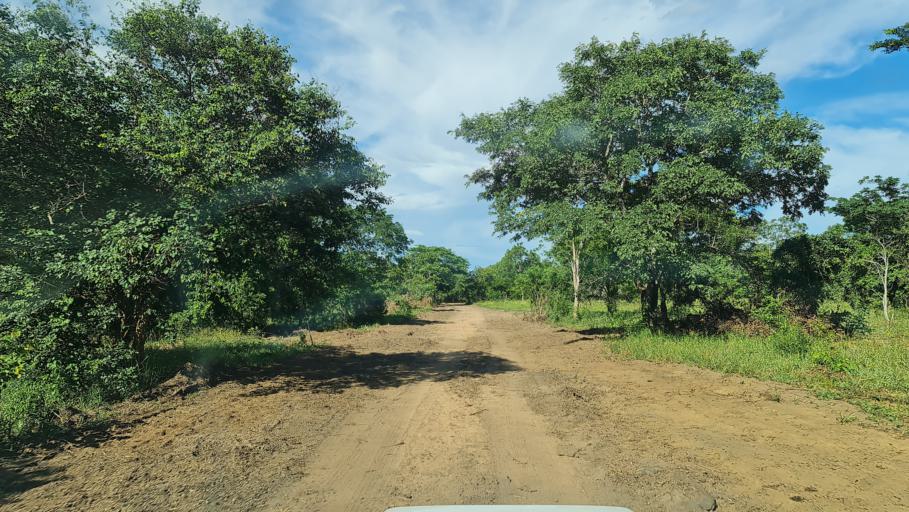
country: MZ
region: Nampula
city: Antonio Enes
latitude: -15.5111
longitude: 40.1330
